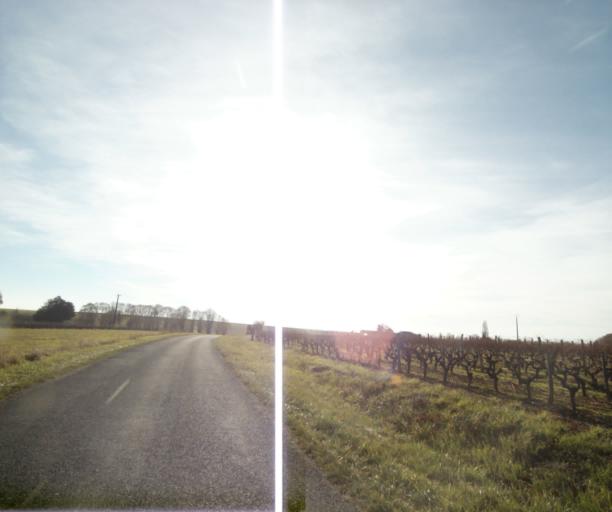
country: FR
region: Poitou-Charentes
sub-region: Departement de la Charente-Maritime
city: Chaniers
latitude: 45.7335
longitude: -0.5489
